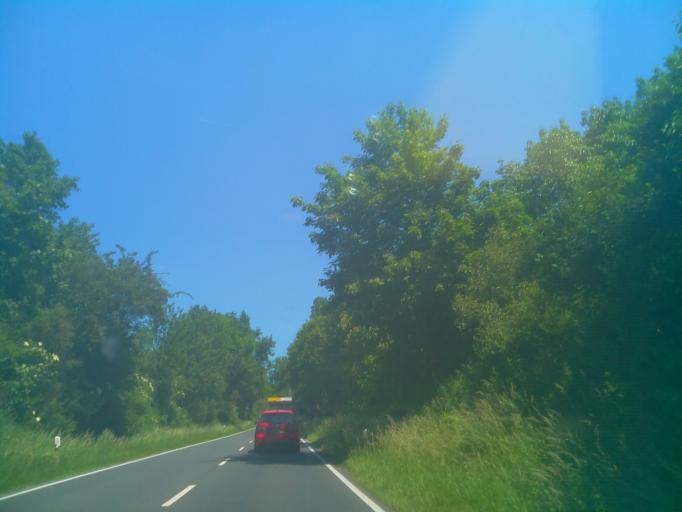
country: DE
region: Bavaria
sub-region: Regierungsbezirk Unterfranken
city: Schweinfurt
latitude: 50.0582
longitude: 10.2390
